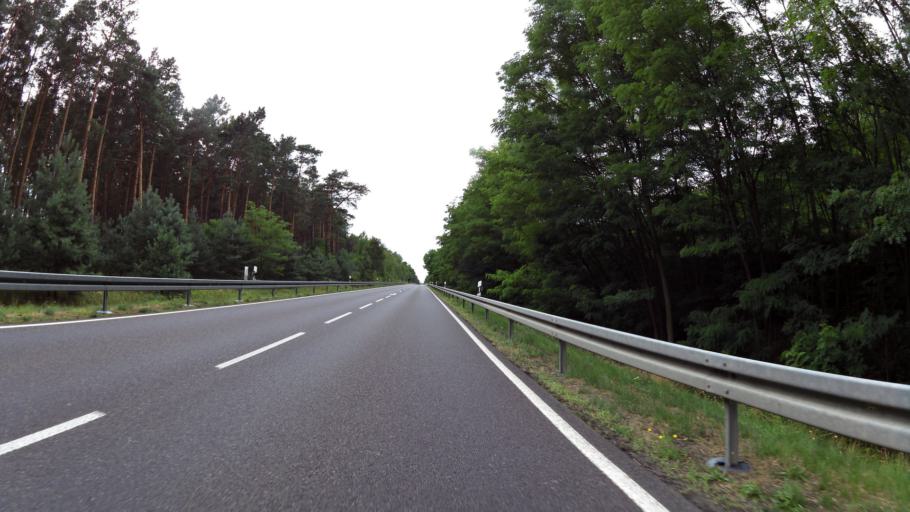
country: DE
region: Brandenburg
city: Schenkendobern
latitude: 51.8967
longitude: 14.5966
